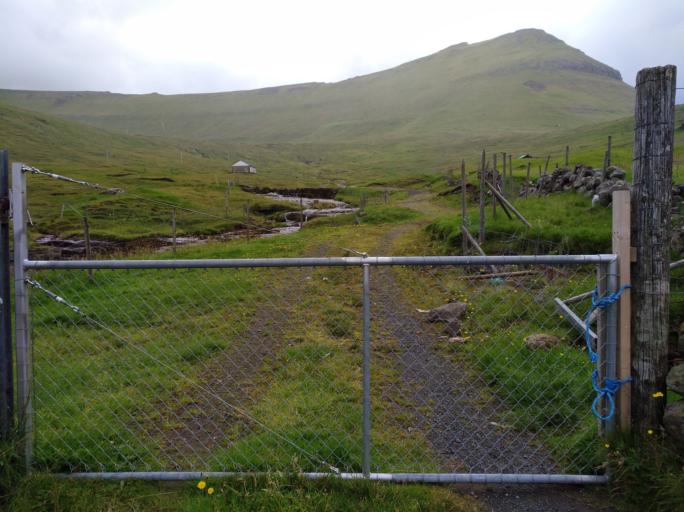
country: FO
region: Eysturoy
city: Fuglafjordur
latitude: 62.2795
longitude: -6.8616
